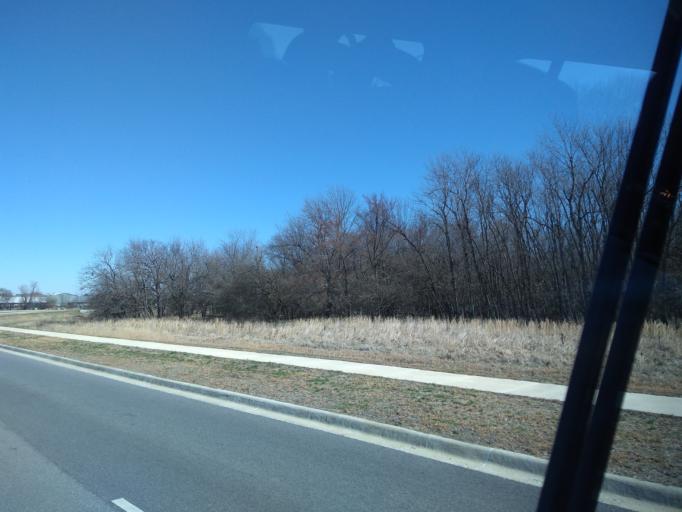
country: US
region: Arkansas
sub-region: Washington County
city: Farmington
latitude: 36.0649
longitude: -94.2202
